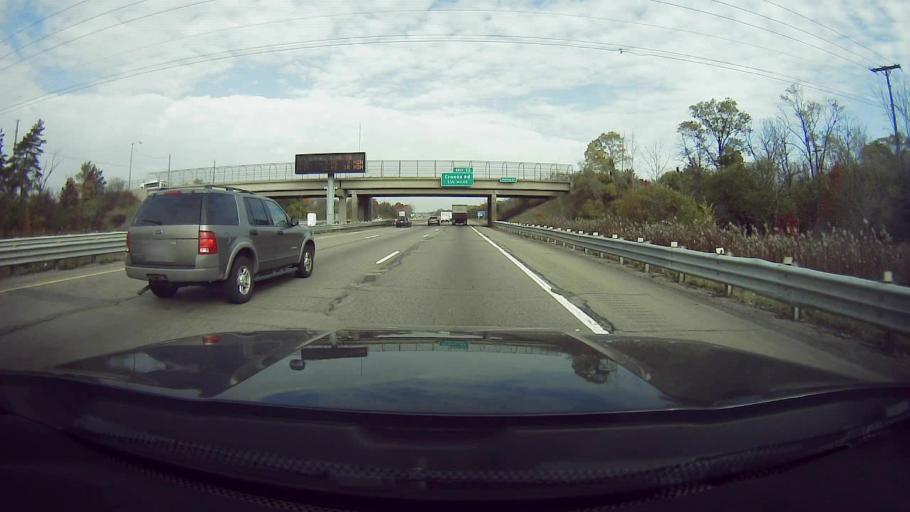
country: US
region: Michigan
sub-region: Oakland County
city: Troy
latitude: 42.5763
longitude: -83.1590
